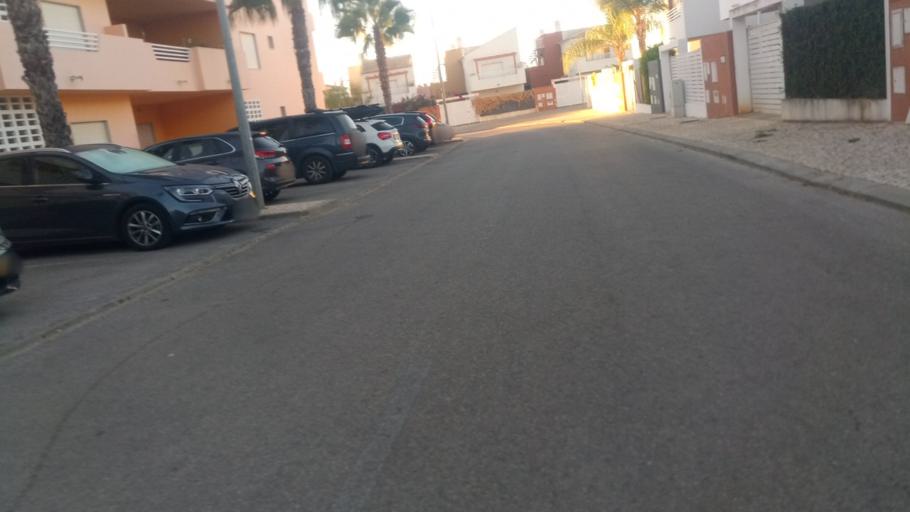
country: PT
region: Faro
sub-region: Tavira
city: Tavira
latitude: 37.1444
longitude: -7.6084
